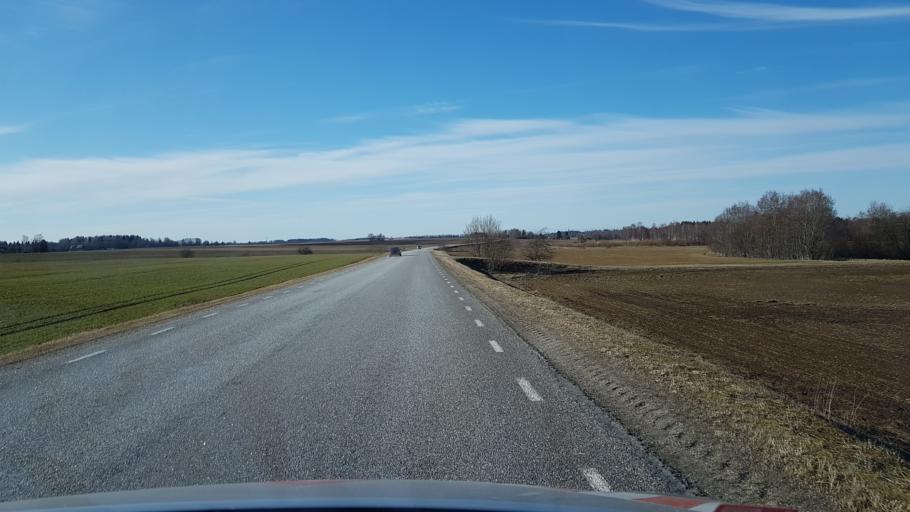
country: EE
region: Laeaene-Virumaa
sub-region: Kadrina vald
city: Kadrina
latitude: 59.3143
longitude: 26.1522
